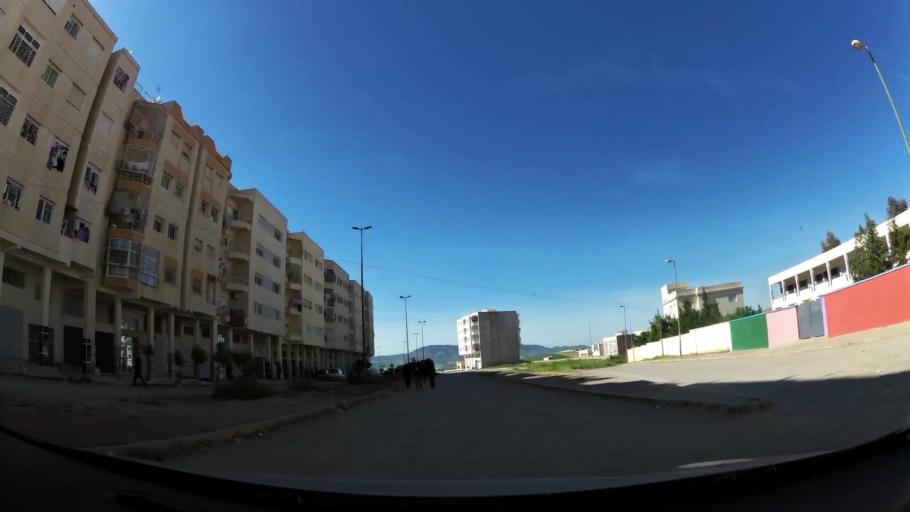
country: MA
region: Fes-Boulemane
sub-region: Fes
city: Fes
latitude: 34.0157
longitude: -4.9597
